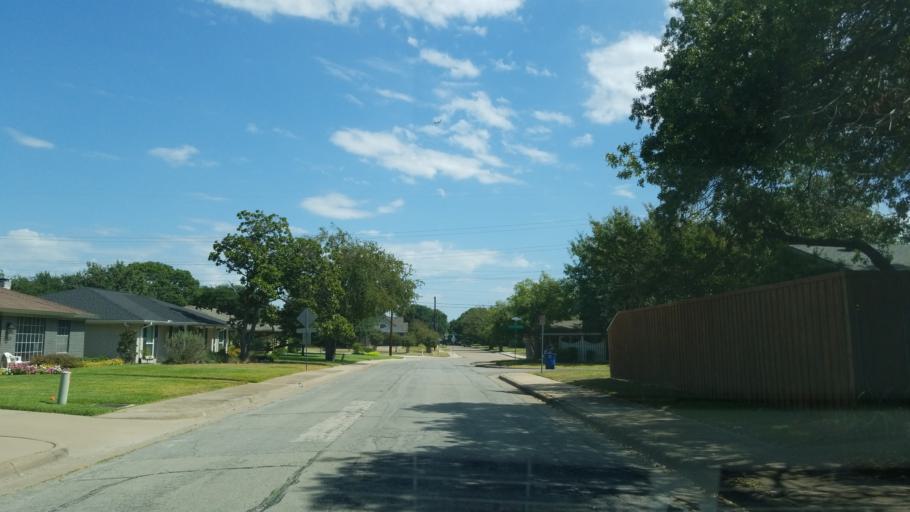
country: US
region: Texas
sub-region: Dallas County
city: Addison
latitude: 32.9645
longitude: -96.7796
